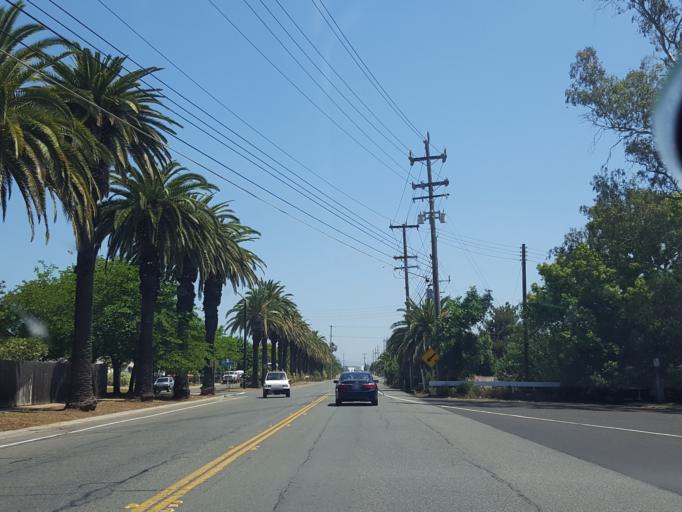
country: US
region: California
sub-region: Sacramento County
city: La Riviera
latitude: 38.5579
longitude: -121.3259
